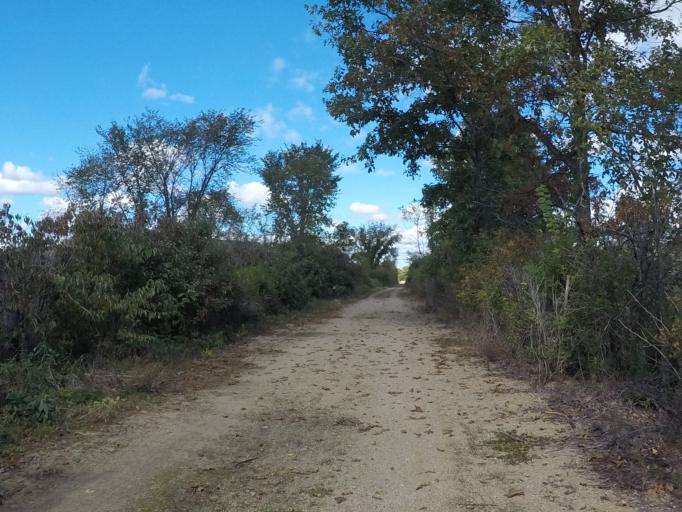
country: US
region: Wisconsin
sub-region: Richland County
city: Richland Center
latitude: 43.2703
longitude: -90.3085
